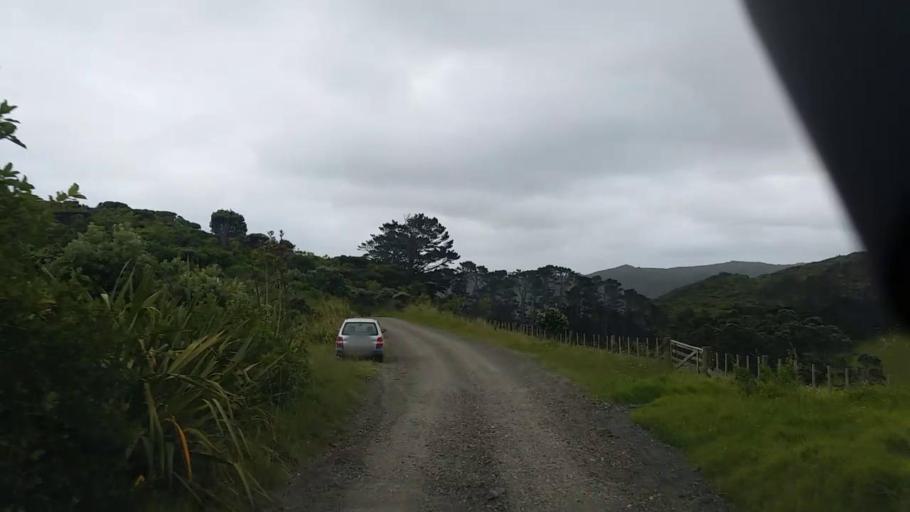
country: NZ
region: Auckland
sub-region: Auckland
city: Muriwai Beach
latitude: -36.9270
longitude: 174.4592
